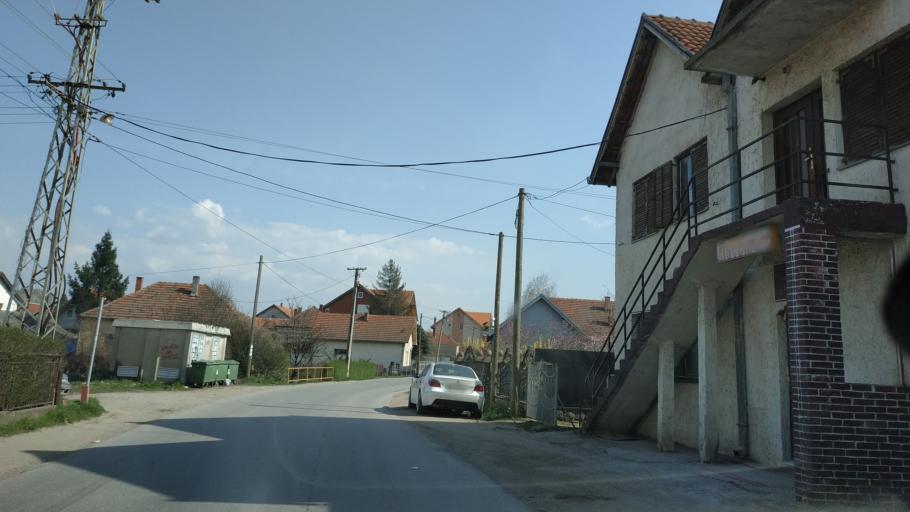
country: RS
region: Central Serbia
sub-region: Nisavski Okrug
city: Aleksinac
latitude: 43.5112
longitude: 21.6909
